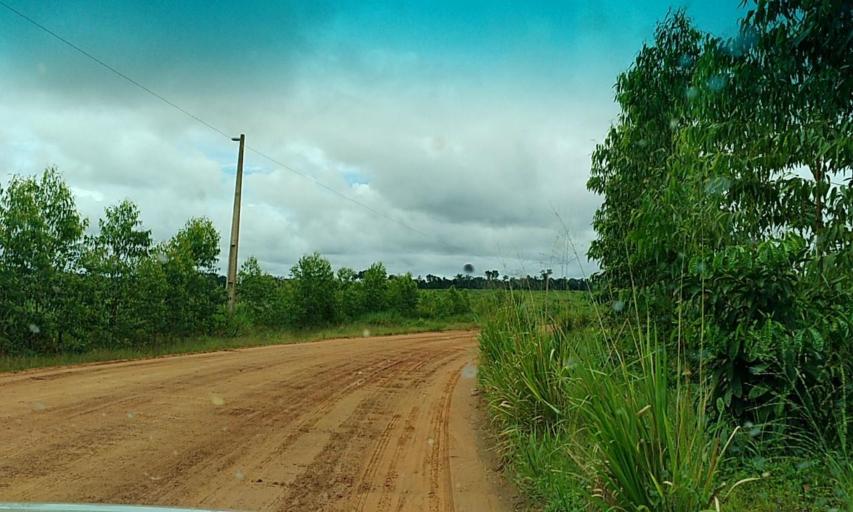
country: BR
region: Para
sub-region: Altamira
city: Altamira
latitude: -3.0590
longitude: -51.7231
